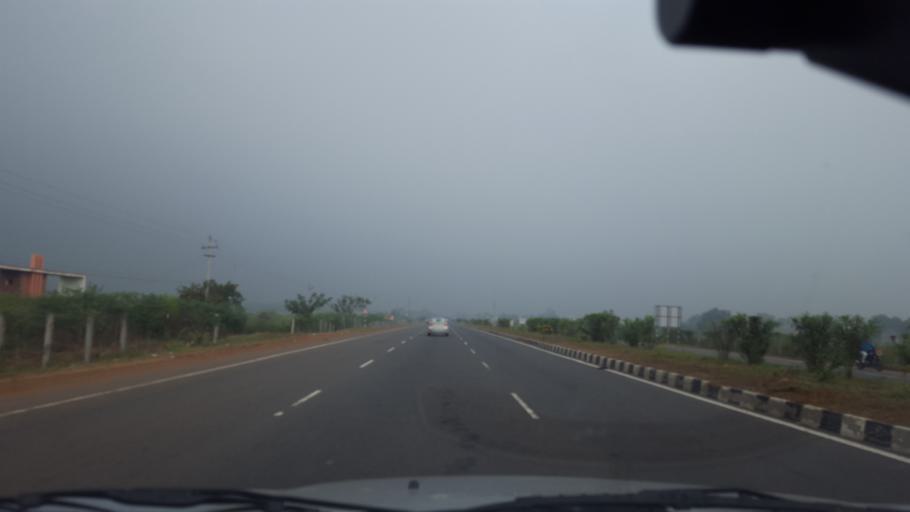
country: IN
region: Andhra Pradesh
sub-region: Prakasam
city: Ongole
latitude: 15.5788
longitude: 80.0416
